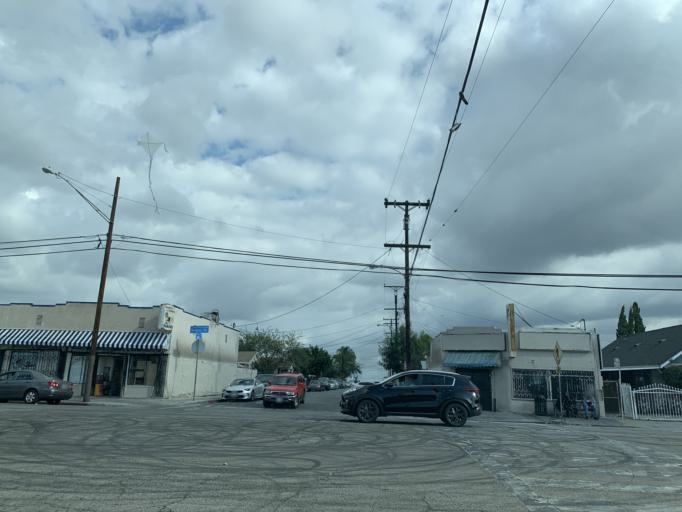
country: US
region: California
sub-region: Los Angeles County
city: Florence-Graham
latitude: 33.9796
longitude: -118.2413
